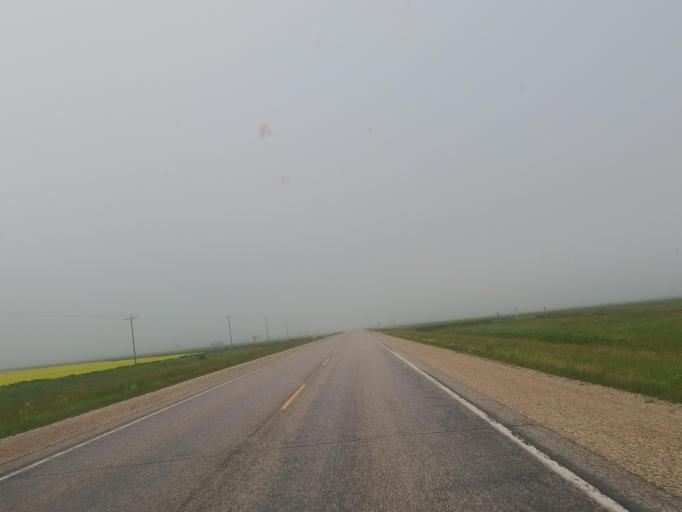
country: CA
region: Manitoba
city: Carman
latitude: 49.6926
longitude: -97.9587
